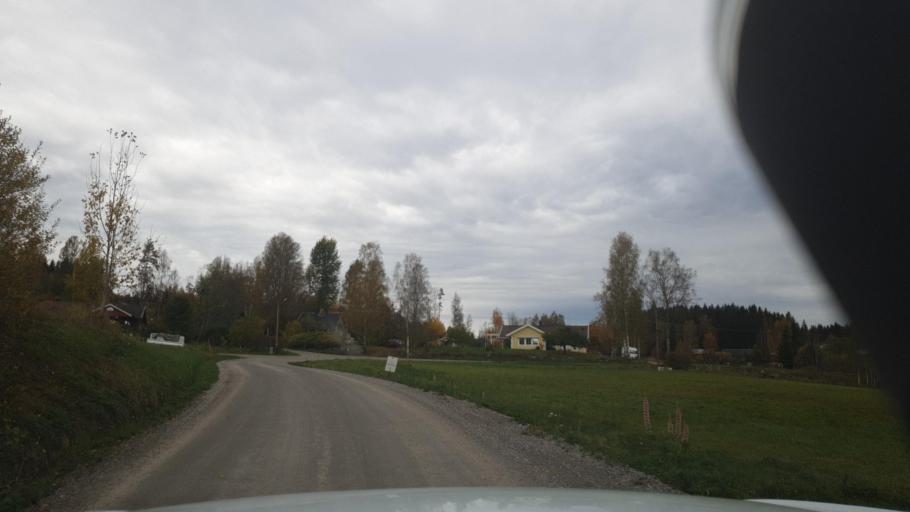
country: SE
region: Vaermland
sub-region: Arvika Kommun
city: Arvika
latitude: 59.6658
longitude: 12.7586
